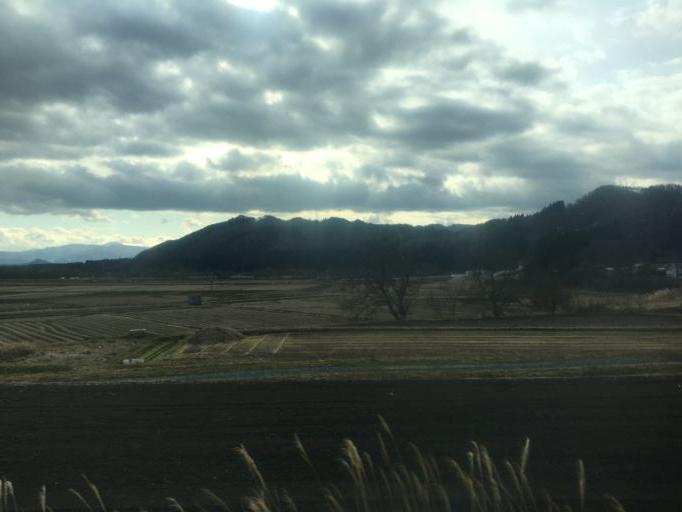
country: JP
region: Akita
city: Odate
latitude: 40.2732
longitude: 140.4727
